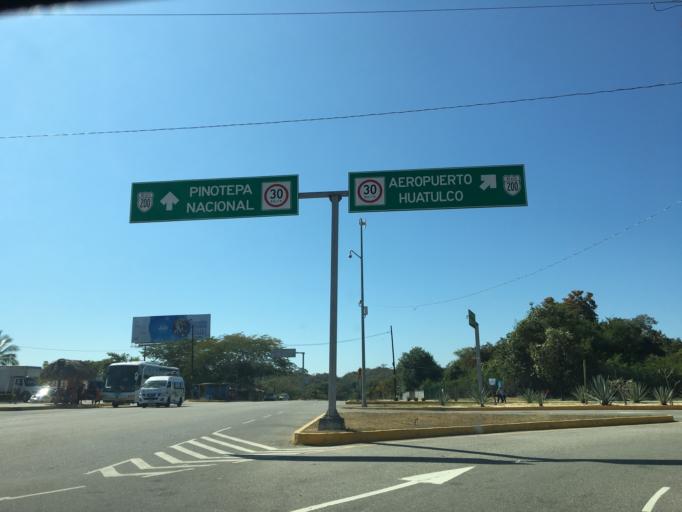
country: MX
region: Oaxaca
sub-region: Santa Maria Huatulco
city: Cuapinolito (Azulillo)
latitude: 15.7683
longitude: -96.2578
